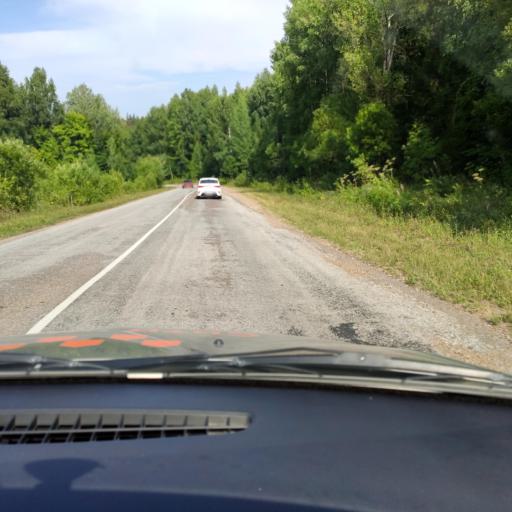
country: RU
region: Bashkortostan
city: Pavlovka
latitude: 55.4066
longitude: 56.5764
